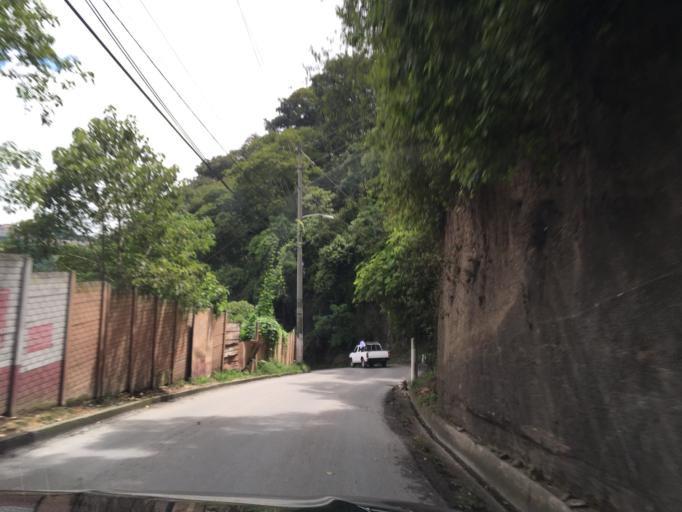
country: GT
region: Guatemala
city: Mixco
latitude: 14.6242
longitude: -90.5854
